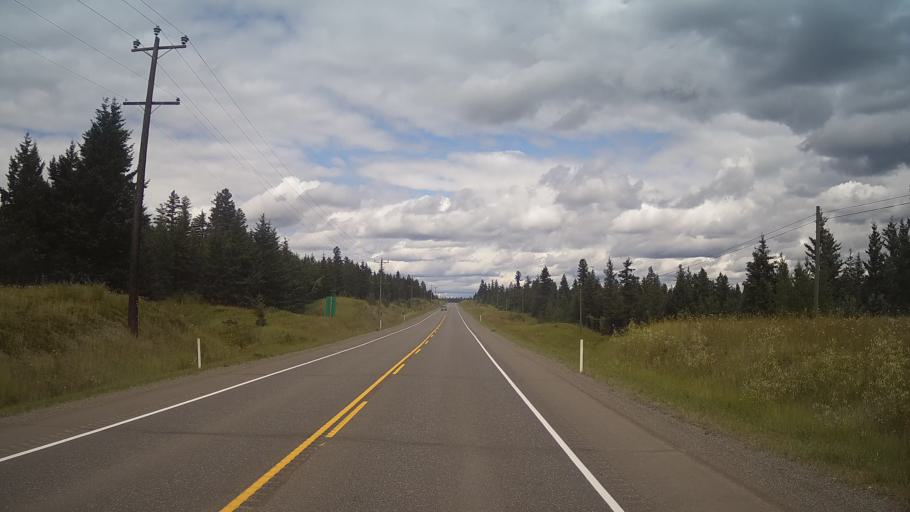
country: CA
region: British Columbia
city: Cache Creek
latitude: 51.1639
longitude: -121.5046
